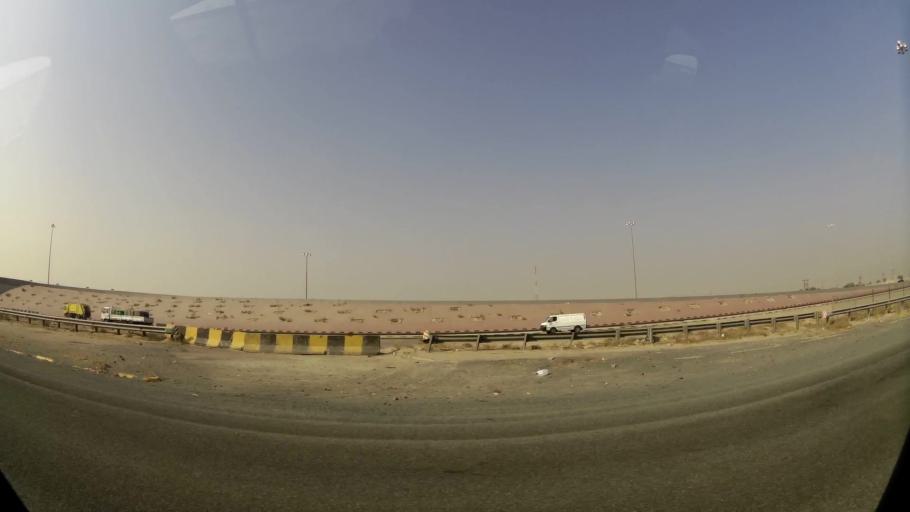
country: KW
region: Al Asimah
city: Ar Rabiyah
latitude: 29.2364
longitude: 47.8828
